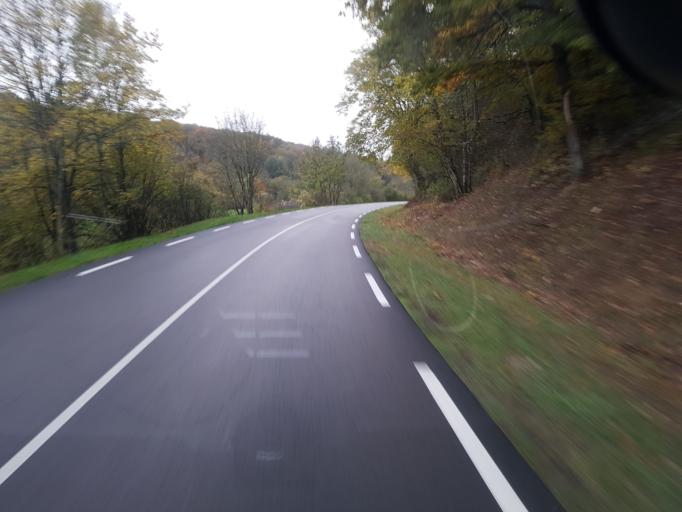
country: FR
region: Bourgogne
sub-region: Departement de la Cote-d'Or
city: Chatillon-sur-Seine
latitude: 47.6745
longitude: 4.7130
